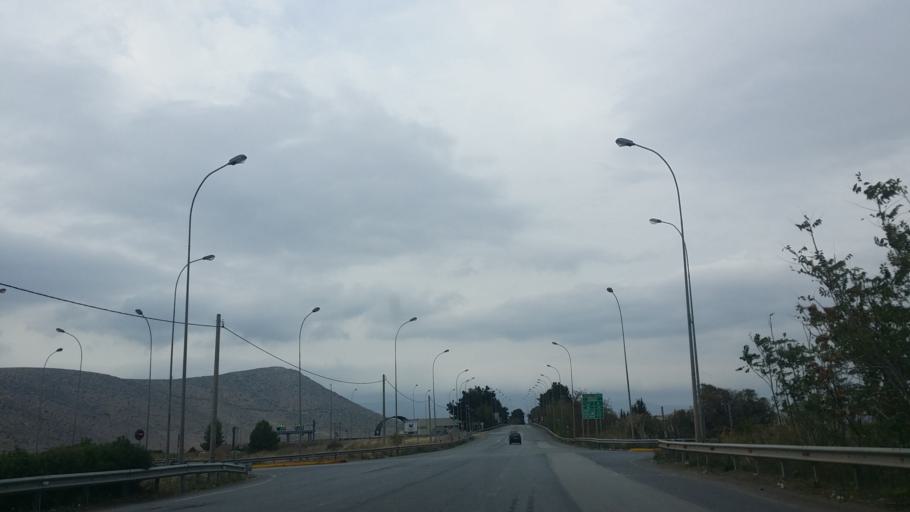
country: GR
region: Central Greece
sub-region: Nomos Voiotias
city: Thivai
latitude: 38.3612
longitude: 23.3226
